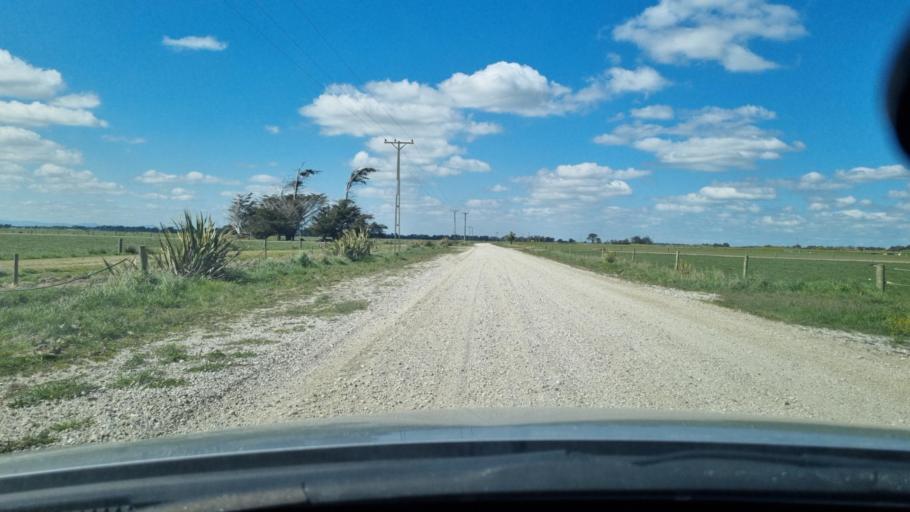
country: NZ
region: Southland
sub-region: Invercargill City
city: Invercargill
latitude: -46.3921
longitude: 168.2520
